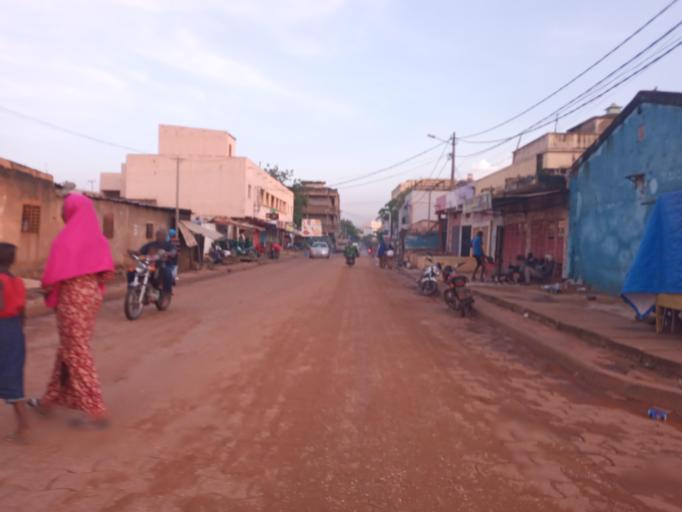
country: ML
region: Bamako
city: Bamako
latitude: 12.6408
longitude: -8.0305
